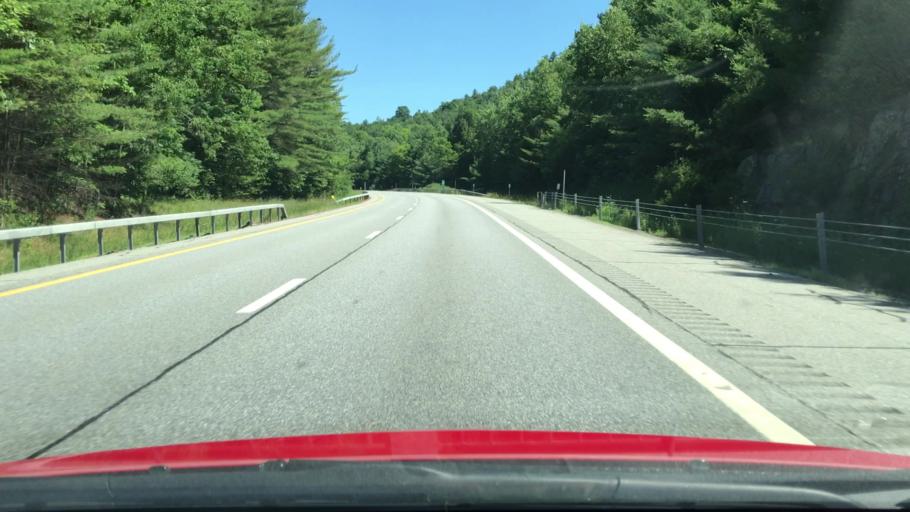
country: US
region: New York
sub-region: Warren County
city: Warrensburg
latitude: 43.5039
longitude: -73.7443
